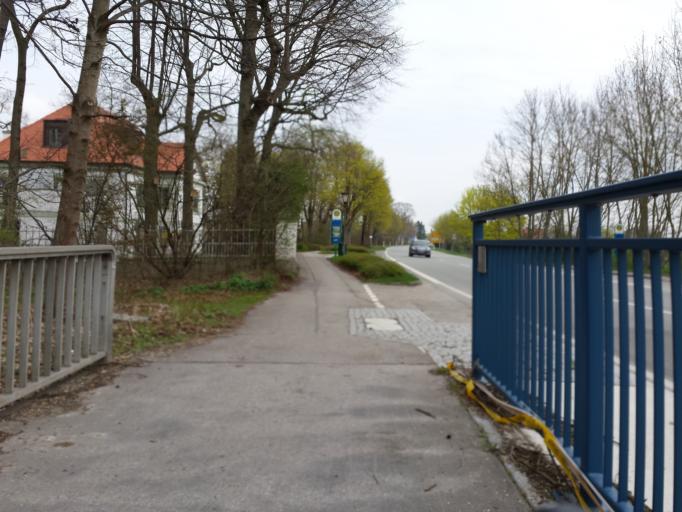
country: DE
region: Bavaria
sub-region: Upper Bavaria
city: Garching bei Munchen
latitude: 48.2370
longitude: 11.6420
